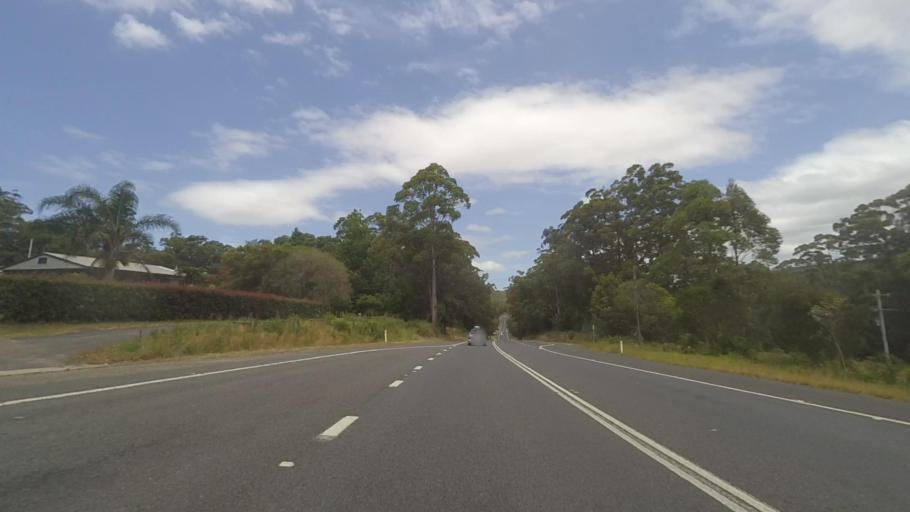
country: AU
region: New South Wales
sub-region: Shoalhaven Shire
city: Milton
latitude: -35.2233
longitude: 150.4360
